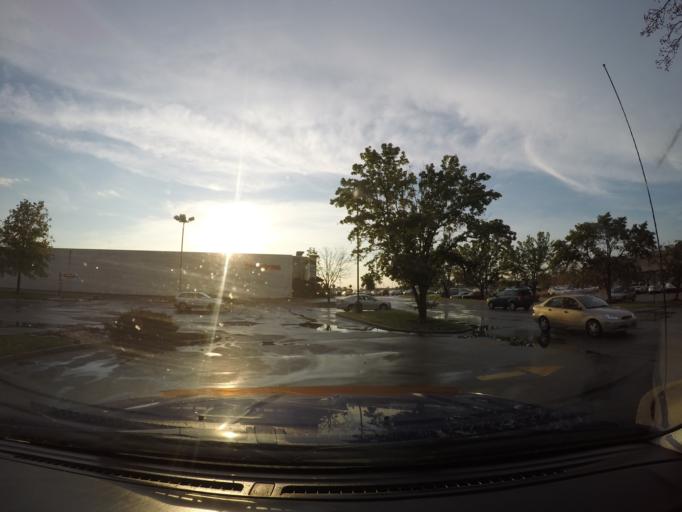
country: US
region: Missouri
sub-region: Saint Louis County
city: Sunset Hills
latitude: 38.5535
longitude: -90.4076
